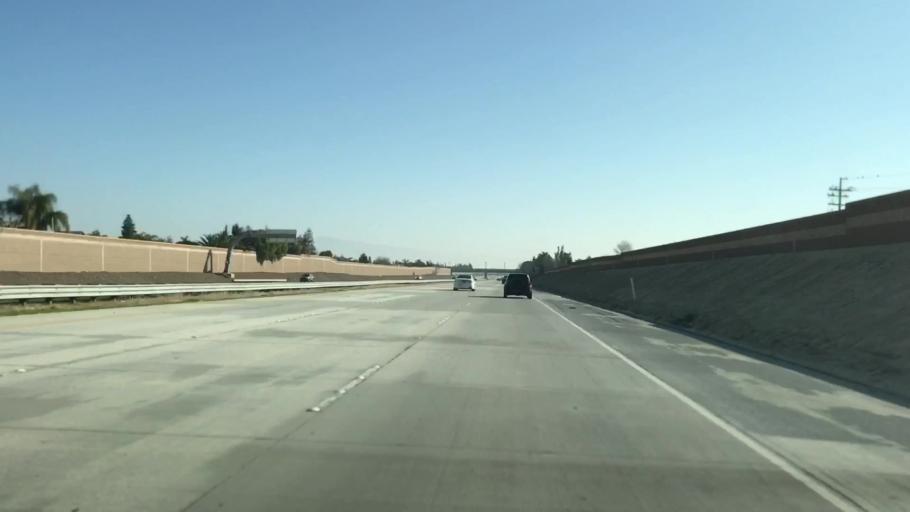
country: US
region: California
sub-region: Kern County
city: Rosedale
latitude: 35.3617
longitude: -119.1366
